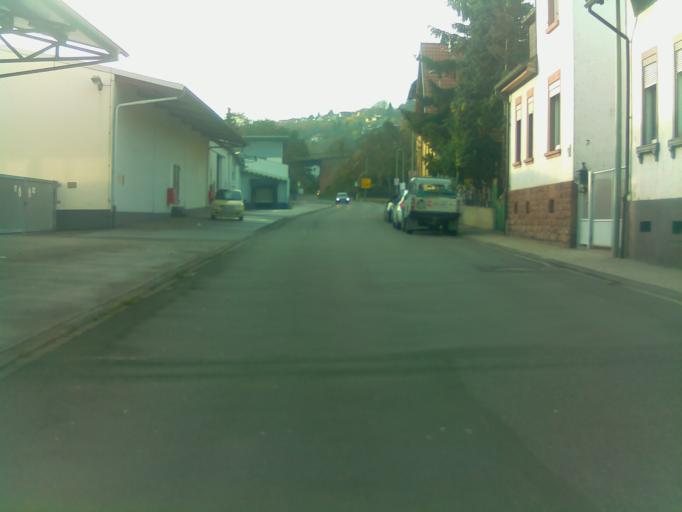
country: DE
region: Rheinland-Pfalz
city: Kleinkarlbach
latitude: 49.5402
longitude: 8.1471
